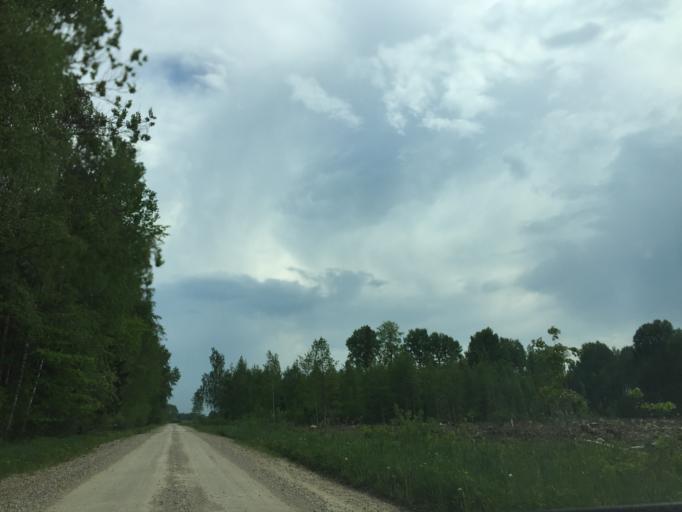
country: LV
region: Livani
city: Livani
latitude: 56.5569
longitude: 26.2242
